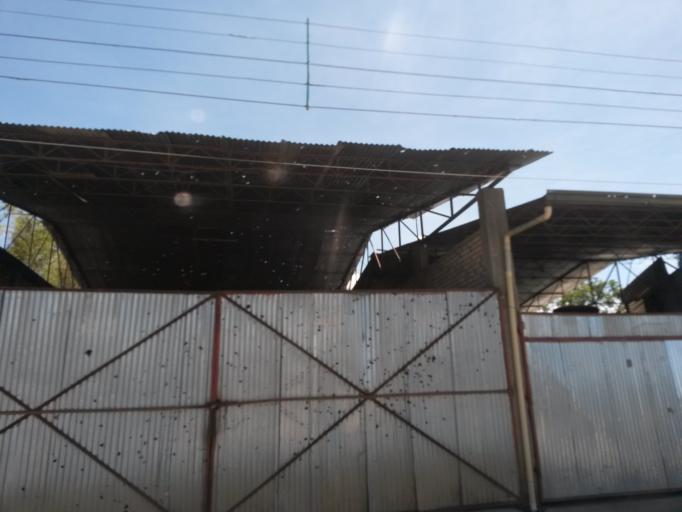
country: CO
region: Cauca
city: El Tambo
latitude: 2.4496
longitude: -76.8151
